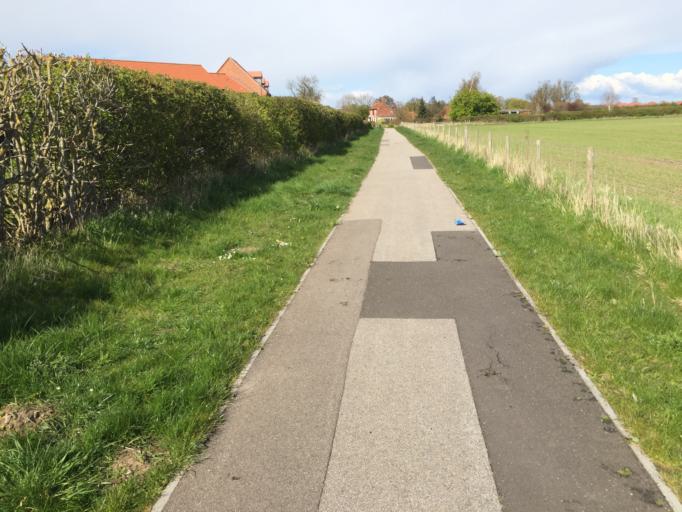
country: GB
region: England
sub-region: Lincolnshire
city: Skellingthorpe
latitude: 53.1233
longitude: -0.6432
